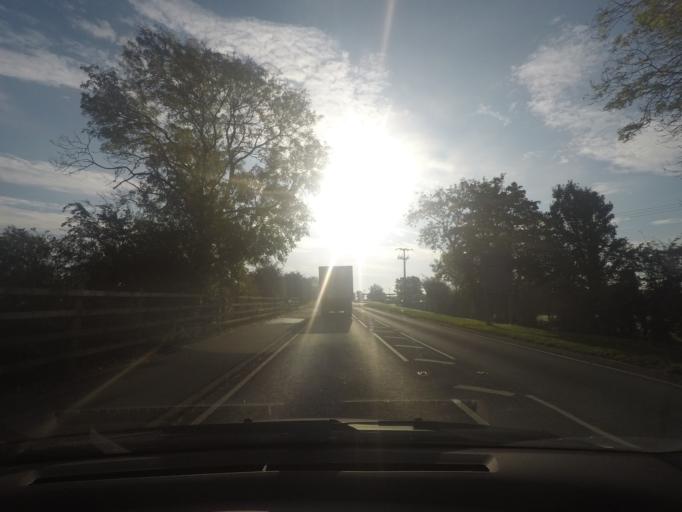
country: GB
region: England
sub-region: East Riding of Yorkshire
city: Londesborough
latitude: 53.8762
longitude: -0.7037
